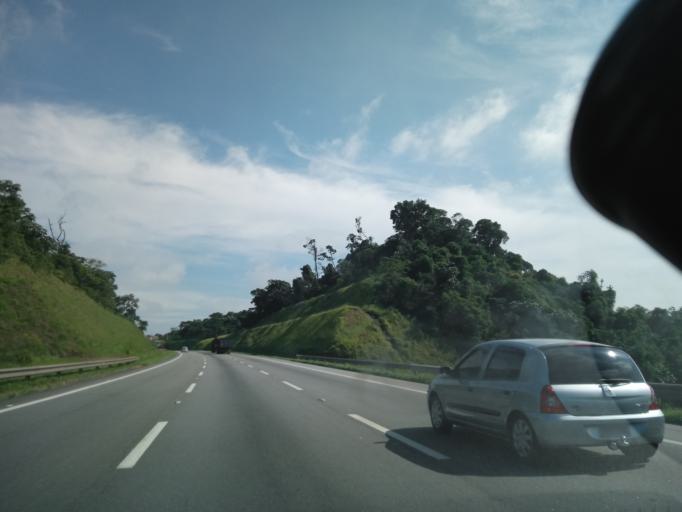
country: BR
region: Sao Paulo
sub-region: Embu
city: Embu
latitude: -23.6658
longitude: -46.8235
